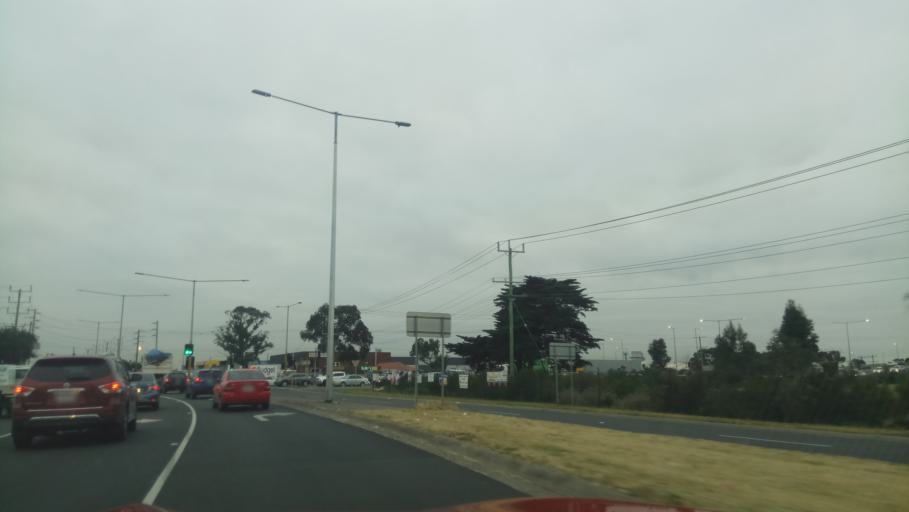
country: AU
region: Victoria
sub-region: Hobsons Bay
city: Laverton
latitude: -37.8449
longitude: 144.7816
